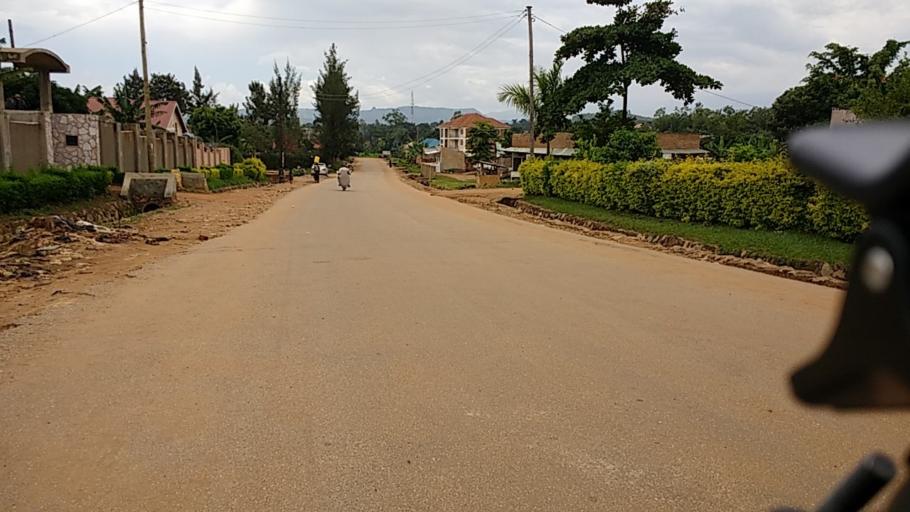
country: UG
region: Eastern Region
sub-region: Mbale District
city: Mbale
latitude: 1.0847
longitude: 34.1726
